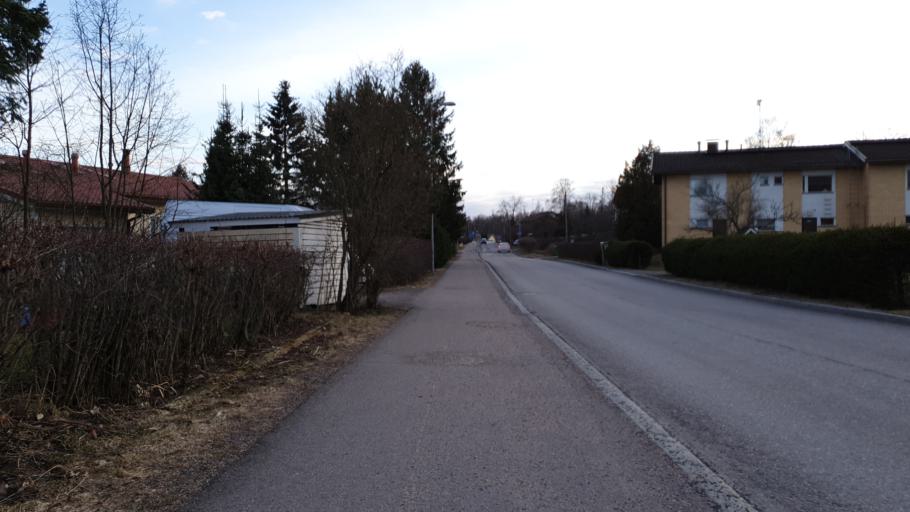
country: FI
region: Uusimaa
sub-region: Helsinki
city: Vantaa
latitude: 60.3122
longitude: 25.0083
